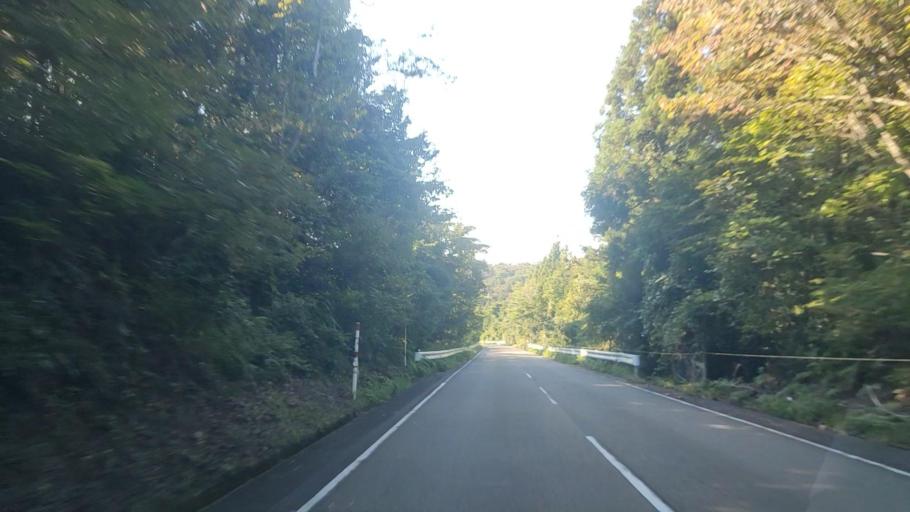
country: JP
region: Ishikawa
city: Nanao
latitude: 37.1185
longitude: 136.9458
